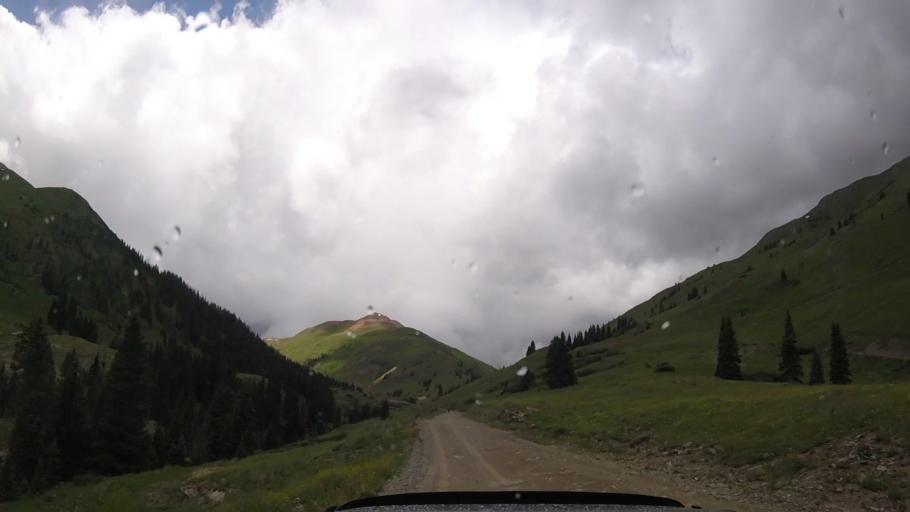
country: US
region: Colorado
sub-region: Ouray County
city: Ouray
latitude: 37.9271
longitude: -107.5640
